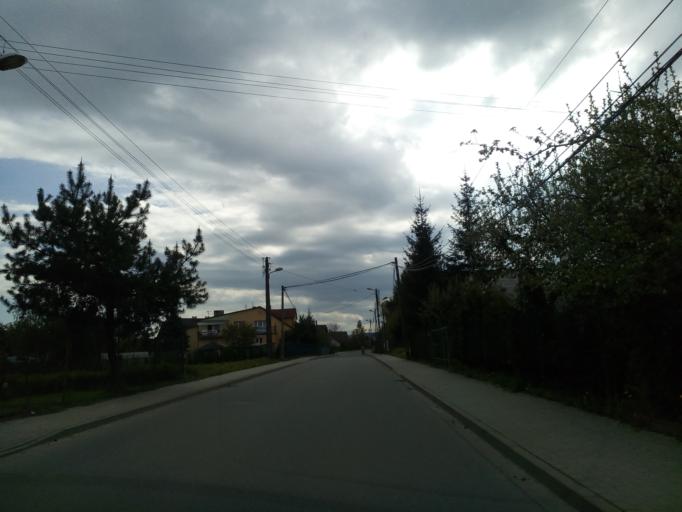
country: PL
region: Lesser Poland Voivodeship
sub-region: Powiat nowosadecki
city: Nowy Sacz
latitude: 49.5917
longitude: 20.7042
